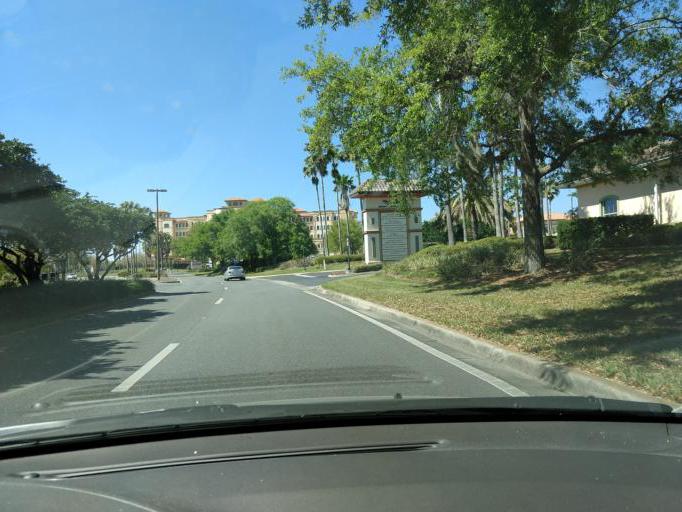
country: US
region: Florida
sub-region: Sumter County
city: The Villages
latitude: 28.9489
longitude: -81.9562
